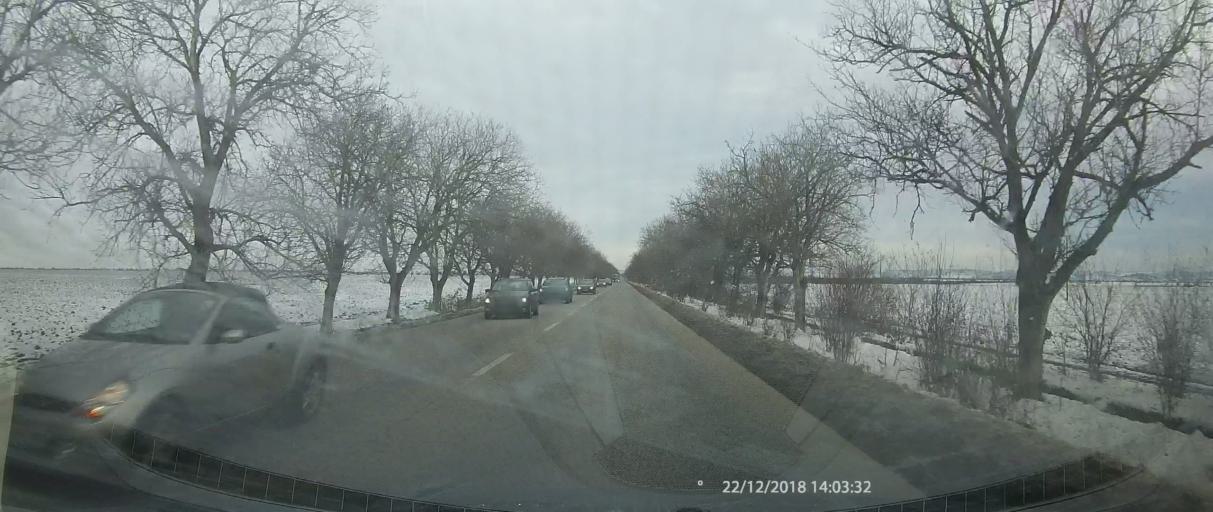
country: BG
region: Pleven
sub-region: Obshtina Dolni Dubnik
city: Dolni Dubnik
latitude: 43.3936
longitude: 24.4093
